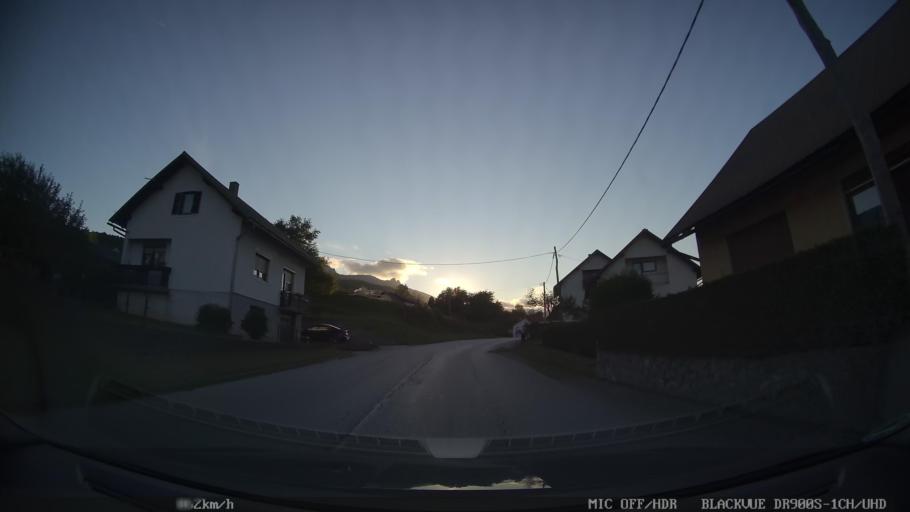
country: HR
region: Karlovacka
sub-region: Grad Ogulin
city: Ogulin
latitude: 45.2681
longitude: 15.1970
